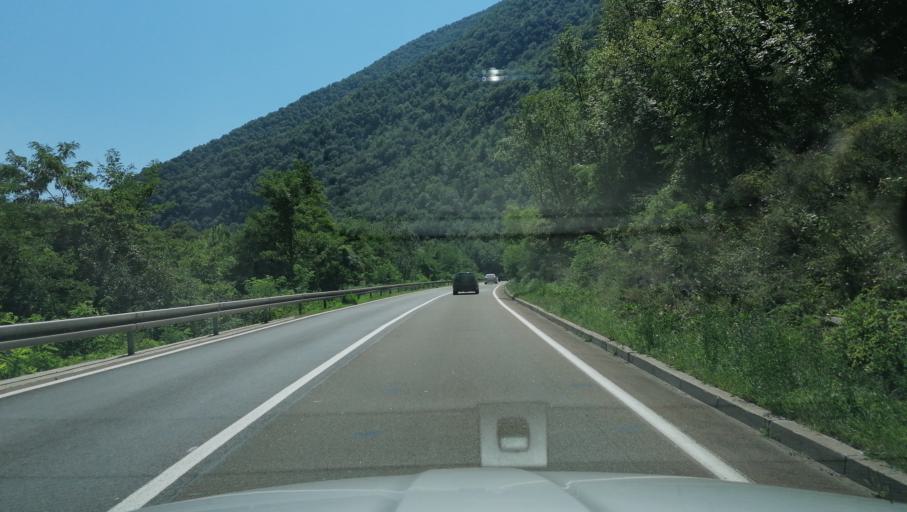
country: RS
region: Central Serbia
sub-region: Raski Okrug
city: Kraljevo
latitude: 43.5734
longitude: 20.5925
